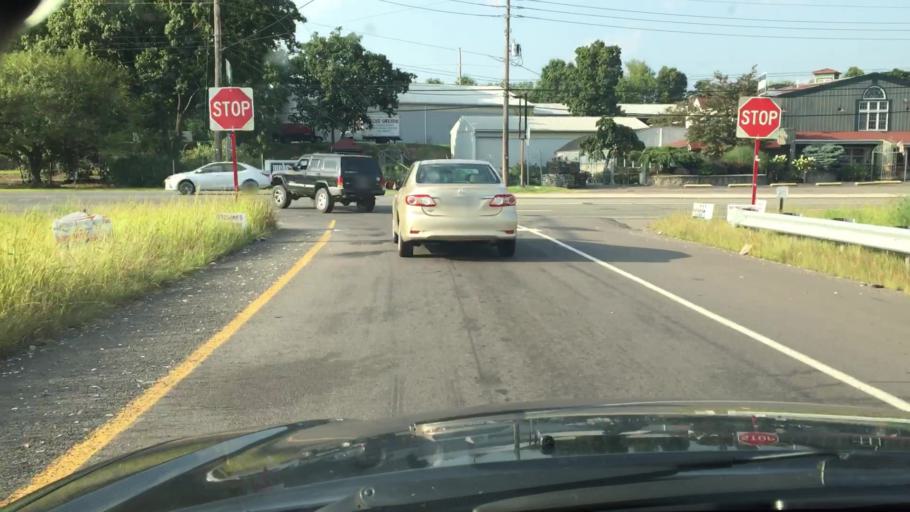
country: US
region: Pennsylvania
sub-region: Luzerne County
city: Nanticoke
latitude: 41.2089
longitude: -75.9784
